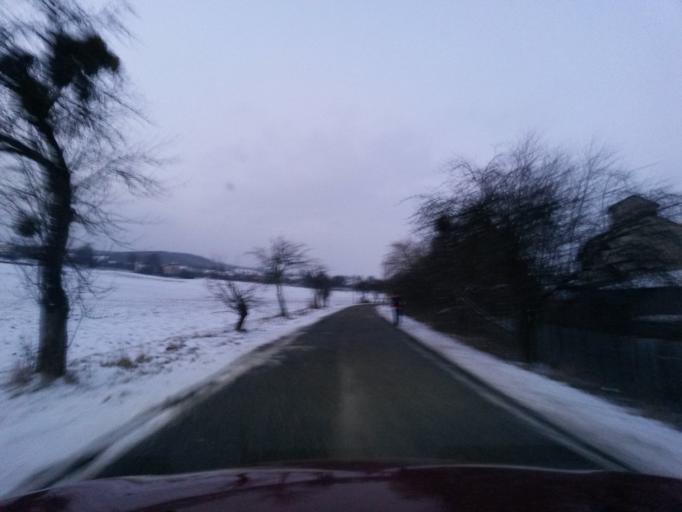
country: SK
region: Kosicky
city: Kosice
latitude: 48.7415
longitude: 21.3237
